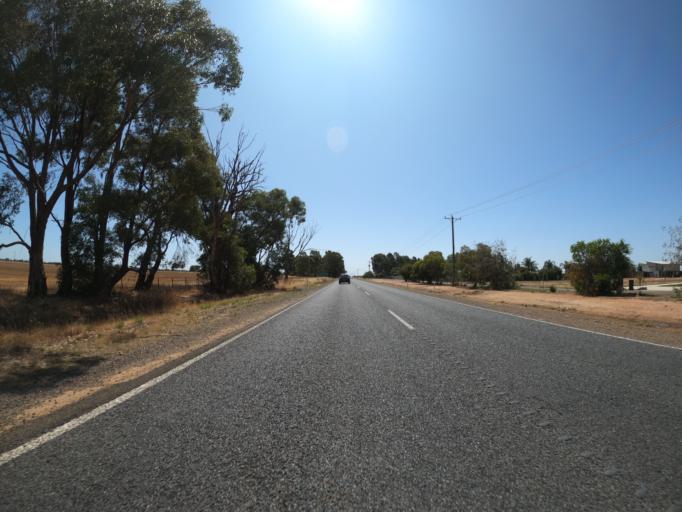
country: AU
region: Victoria
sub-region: Moira
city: Yarrawonga
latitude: -36.0267
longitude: 146.0702
